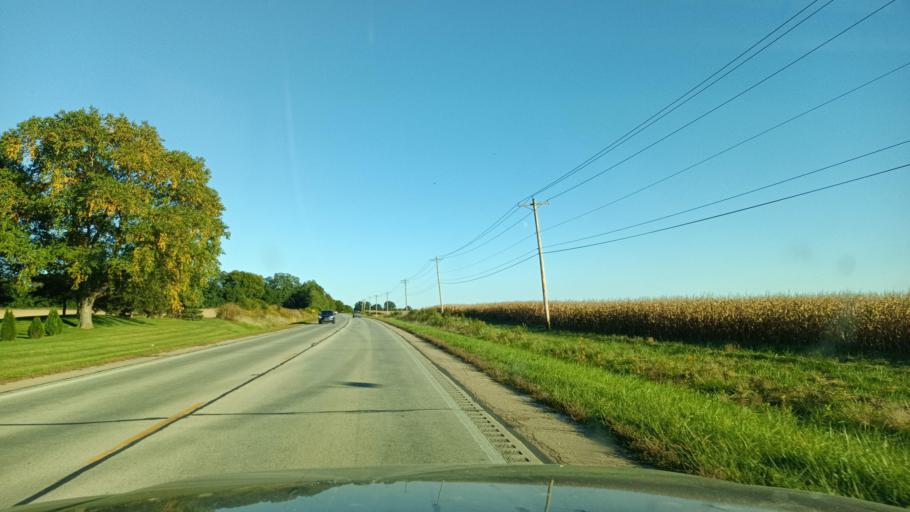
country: US
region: Illinois
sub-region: Champaign County
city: Lake of the Woods
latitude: 40.1649
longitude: -88.3242
